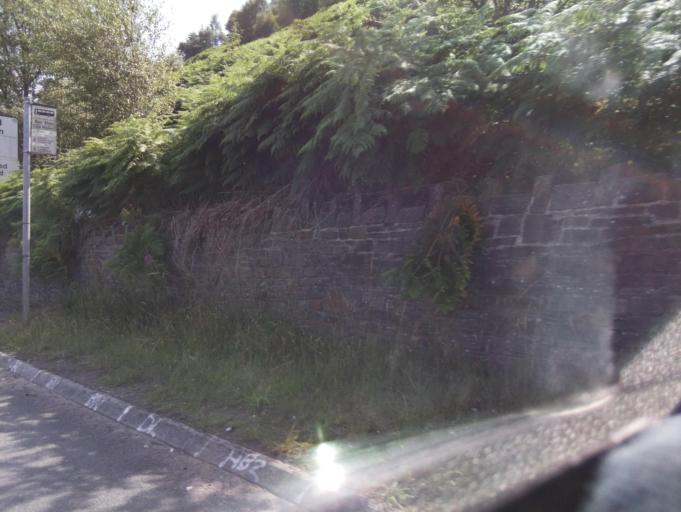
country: GB
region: Wales
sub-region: Caerphilly County Borough
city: New Tredegar
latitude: 51.7238
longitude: -3.2516
